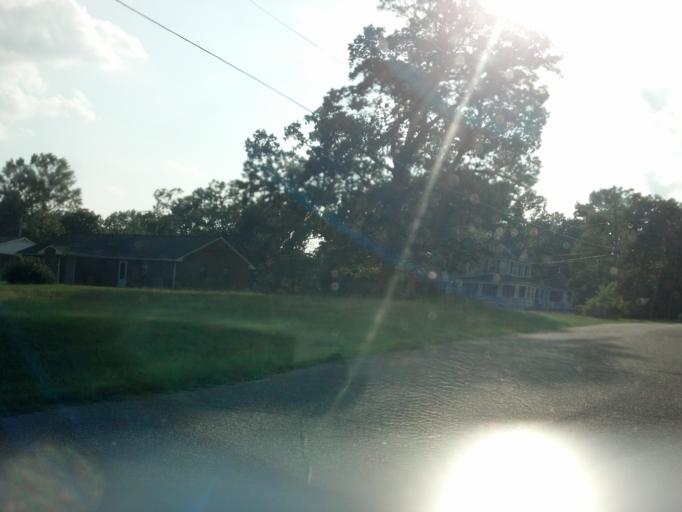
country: US
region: North Carolina
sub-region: Pitt County
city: Ayden
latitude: 35.4732
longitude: -77.4091
